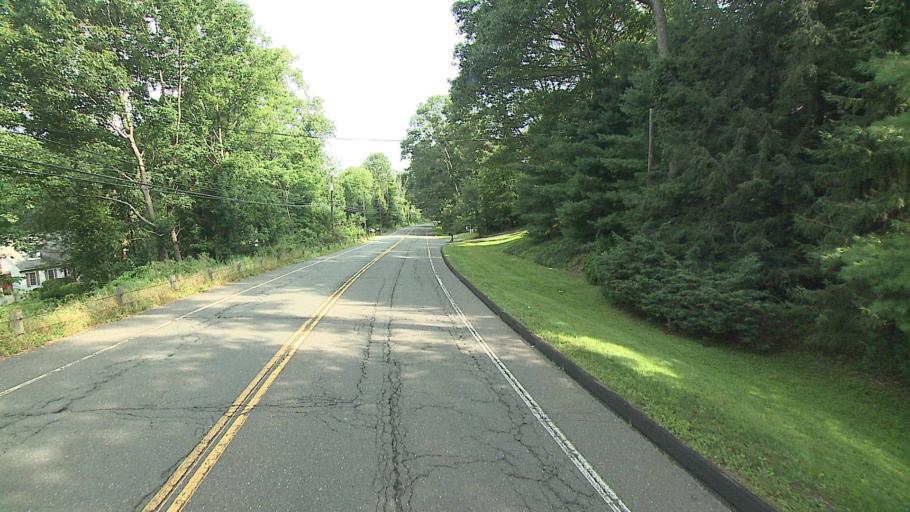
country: US
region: New York
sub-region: Putnam County
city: Putnam Lake
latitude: 41.4755
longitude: -73.4977
